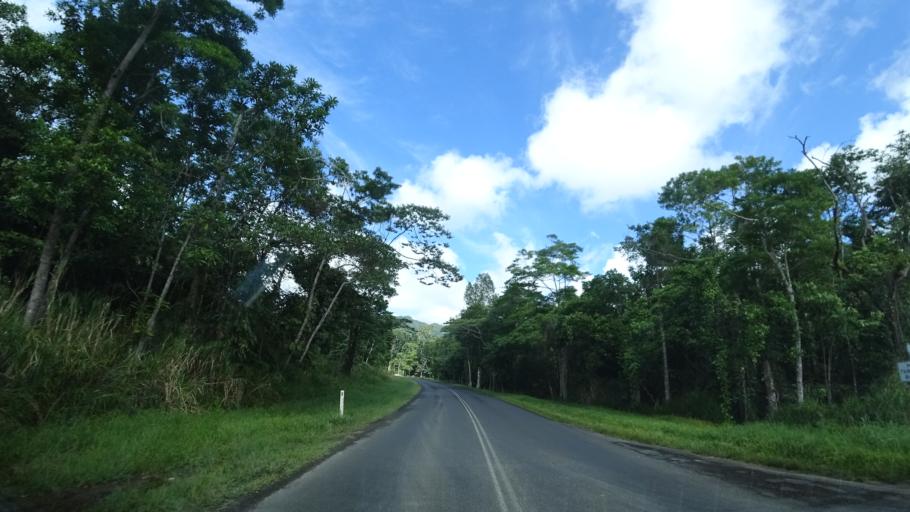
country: AU
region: Queensland
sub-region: Cairns
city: Port Douglas
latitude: -16.2087
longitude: 145.4049
